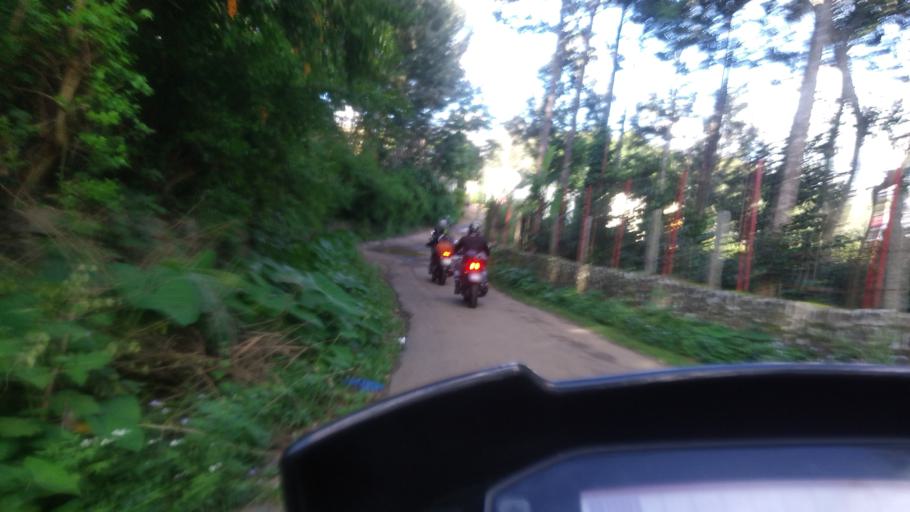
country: IN
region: Tamil Nadu
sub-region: Salem
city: Salem
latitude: 11.7702
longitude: 78.2119
